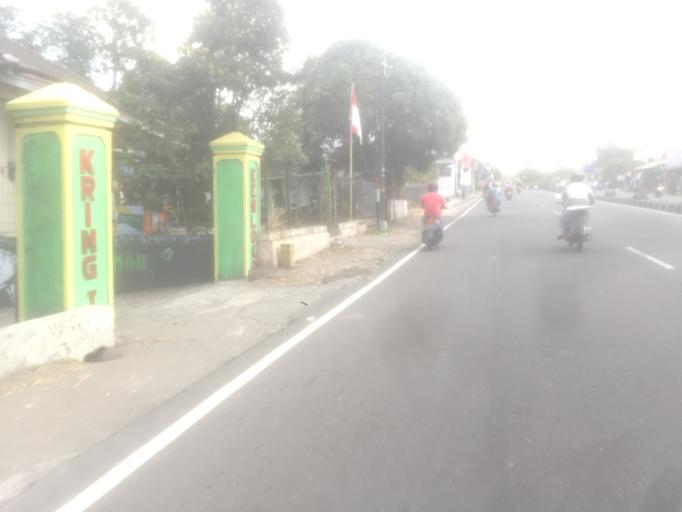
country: ID
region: Daerah Istimewa Yogyakarta
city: Sleman
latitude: -7.6751
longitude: 110.3364
